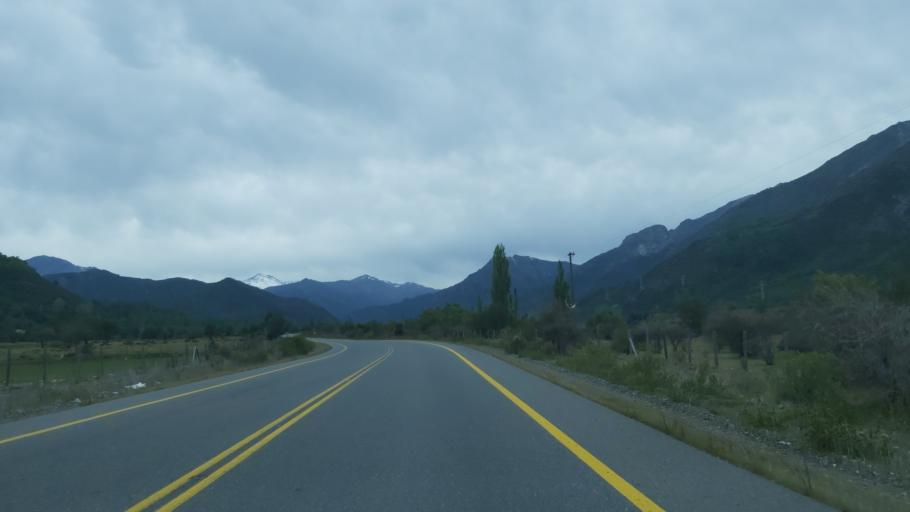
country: CL
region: Maule
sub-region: Provincia de Linares
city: Colbun
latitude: -35.7373
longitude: -71.0112
